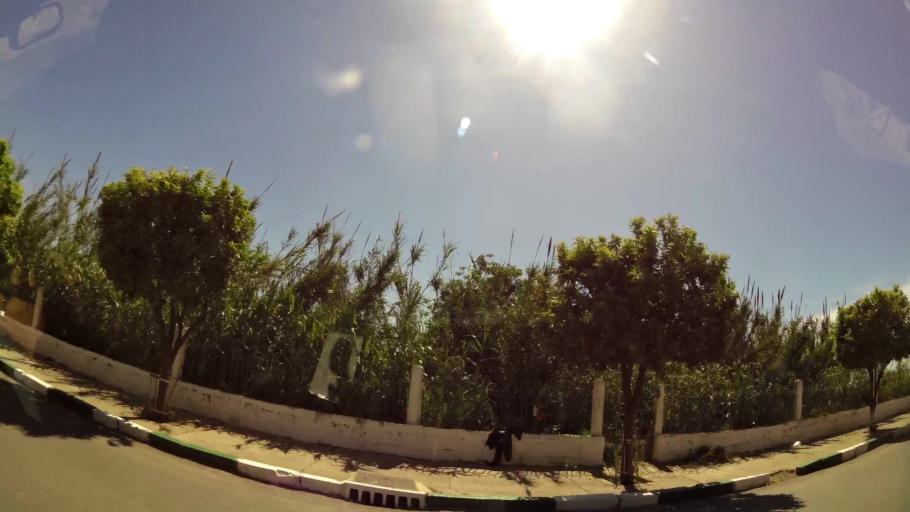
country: MA
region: Meknes-Tafilalet
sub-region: Meknes
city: Meknes
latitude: 33.8903
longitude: -5.5528
